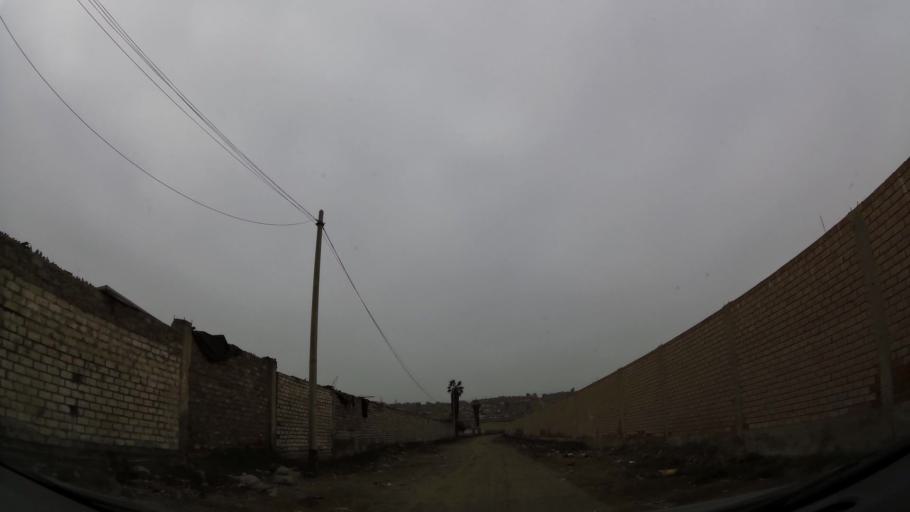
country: PE
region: Lima
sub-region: Lima
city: Surco
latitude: -12.2050
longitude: -76.9864
